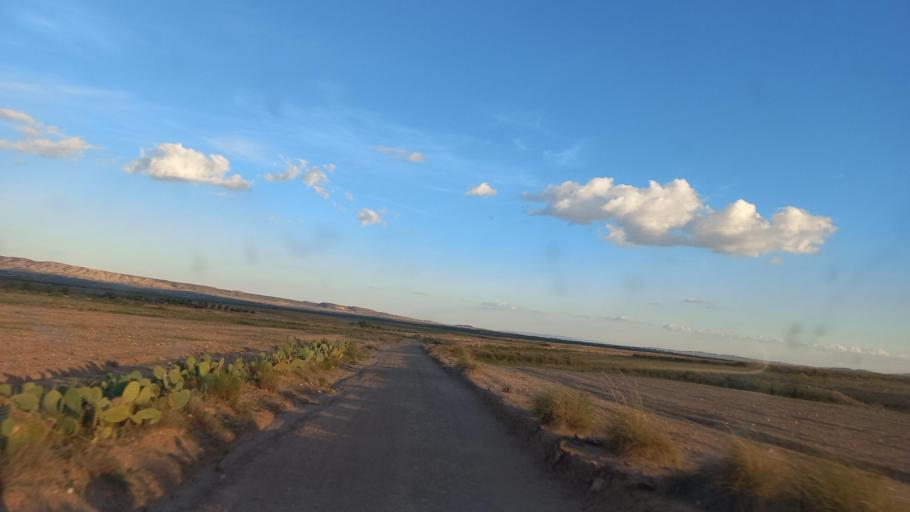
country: TN
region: Al Qasrayn
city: Sbiba
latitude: 35.3504
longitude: 9.0221
